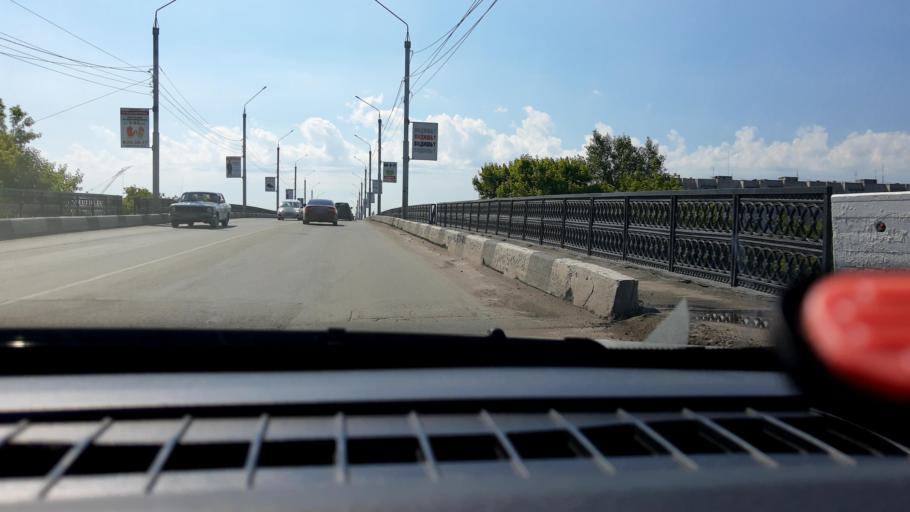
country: RU
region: Nizjnij Novgorod
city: Dzerzhinsk
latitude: 56.2360
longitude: 43.4882
